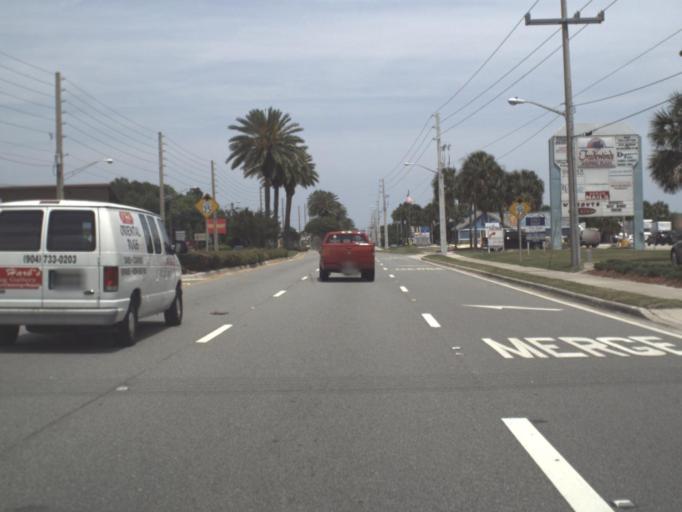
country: US
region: Florida
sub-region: Duval County
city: Atlantic Beach
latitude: 30.3243
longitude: -81.4163
